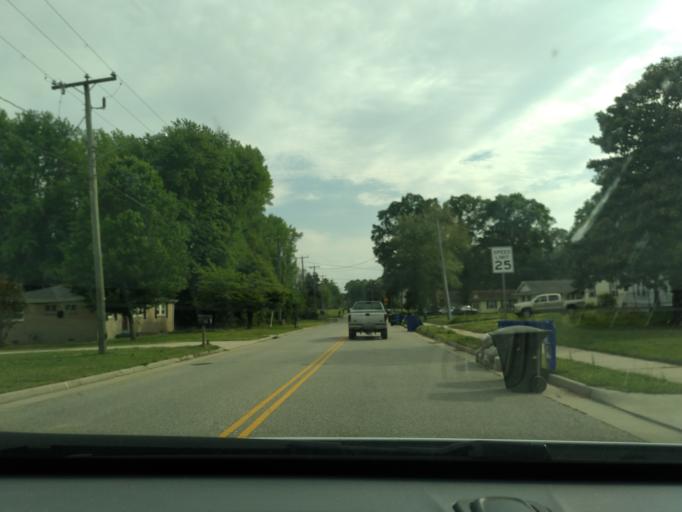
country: US
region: Virginia
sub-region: York County
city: Yorktown
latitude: 37.1654
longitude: -76.5232
